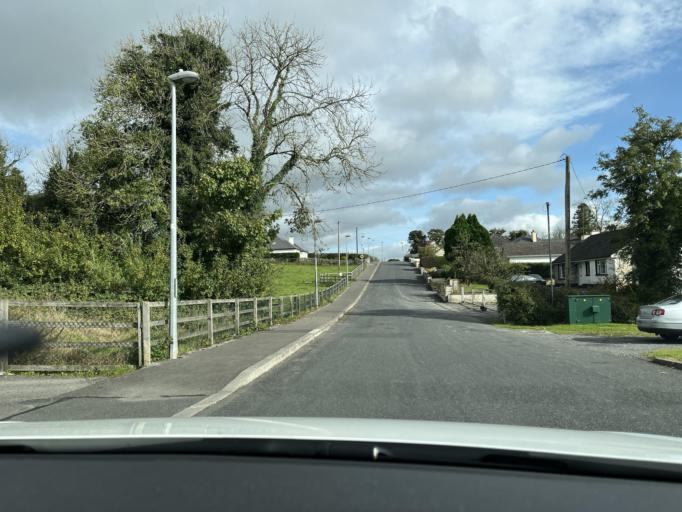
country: IE
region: Connaught
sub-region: County Leitrim
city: Carrick-on-Shannon
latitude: 53.9548
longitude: -8.0694
